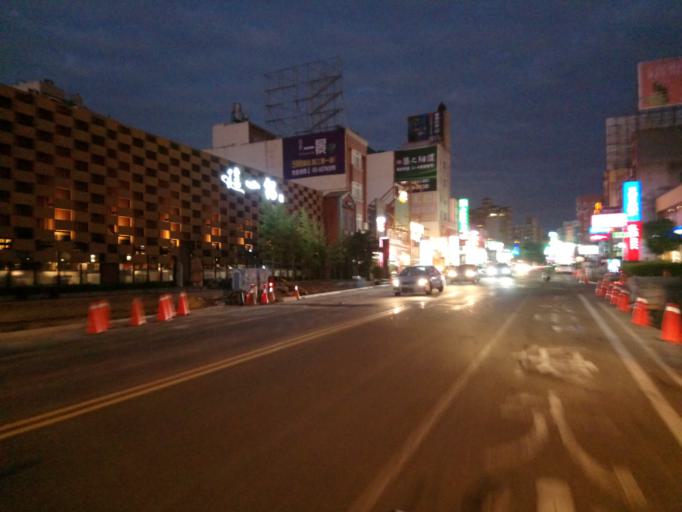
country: TW
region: Taiwan
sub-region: Hsinchu
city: Zhubei
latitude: 24.8306
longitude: 121.0138
